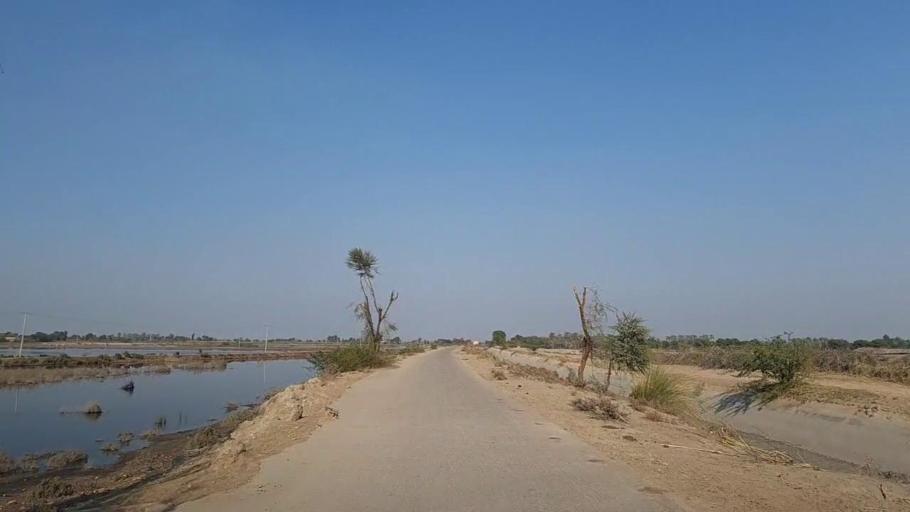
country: PK
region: Sindh
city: Daur
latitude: 26.4296
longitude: 68.2654
